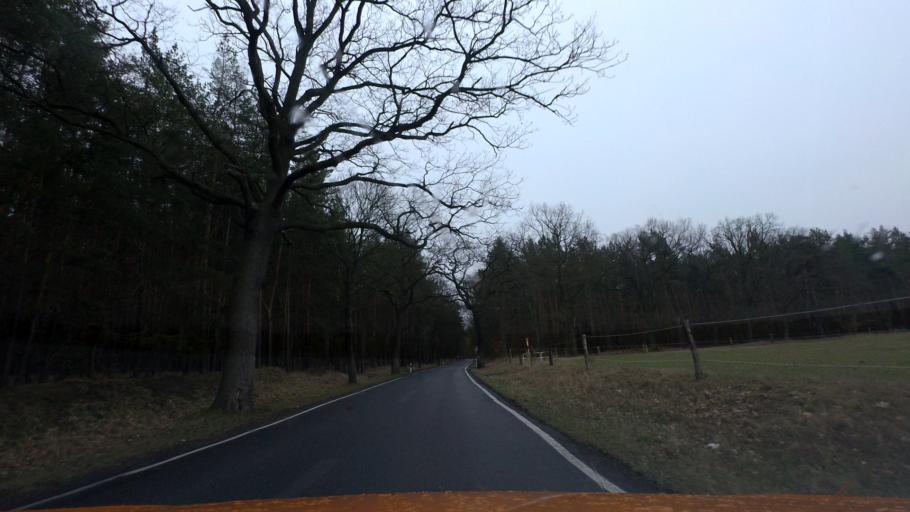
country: DE
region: Brandenburg
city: Brieselang
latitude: 52.6455
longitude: 13.0168
